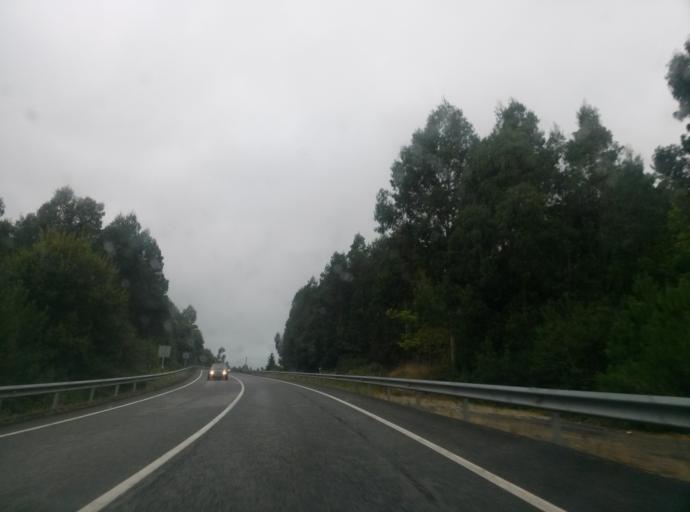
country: ES
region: Galicia
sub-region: Provincia de Lugo
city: Viveiro
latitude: 43.5803
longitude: -7.6338
